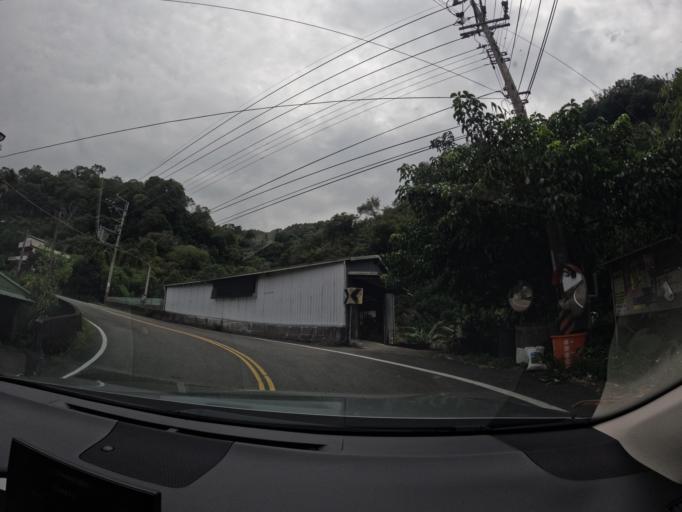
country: TW
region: Taiwan
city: Fengyuan
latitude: 24.3439
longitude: 120.8702
